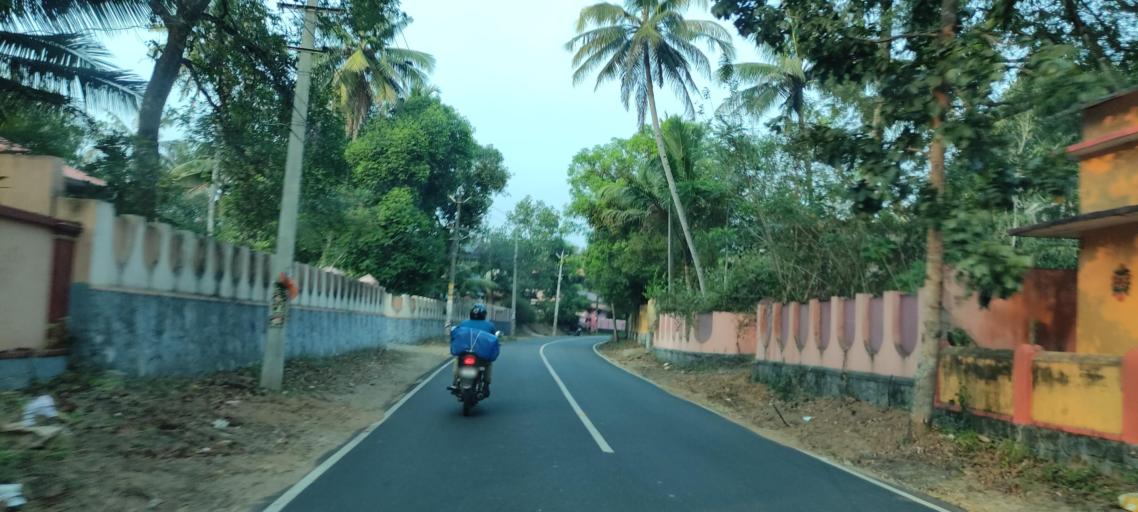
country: IN
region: Kerala
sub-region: Alappuzha
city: Mavelikara
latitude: 9.2611
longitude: 76.5548
